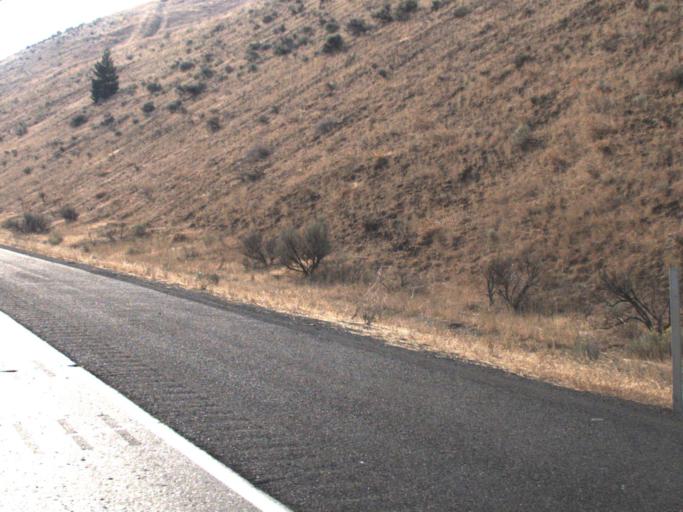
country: US
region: Washington
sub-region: Kittitas County
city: Kittitas
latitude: 46.8929
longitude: -120.4432
